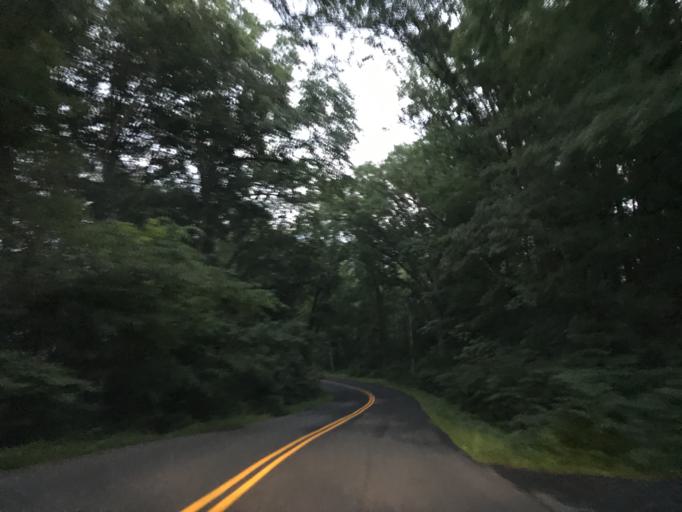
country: US
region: Maryland
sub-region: Harford County
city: Pleasant Hills
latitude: 39.4873
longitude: -76.4149
